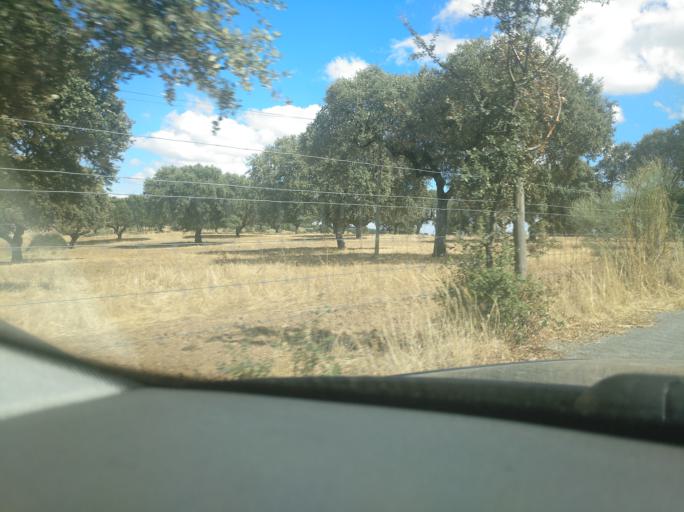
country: ES
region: Extremadura
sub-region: Provincia de Badajoz
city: La Codosera
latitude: 39.1157
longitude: -7.1512
